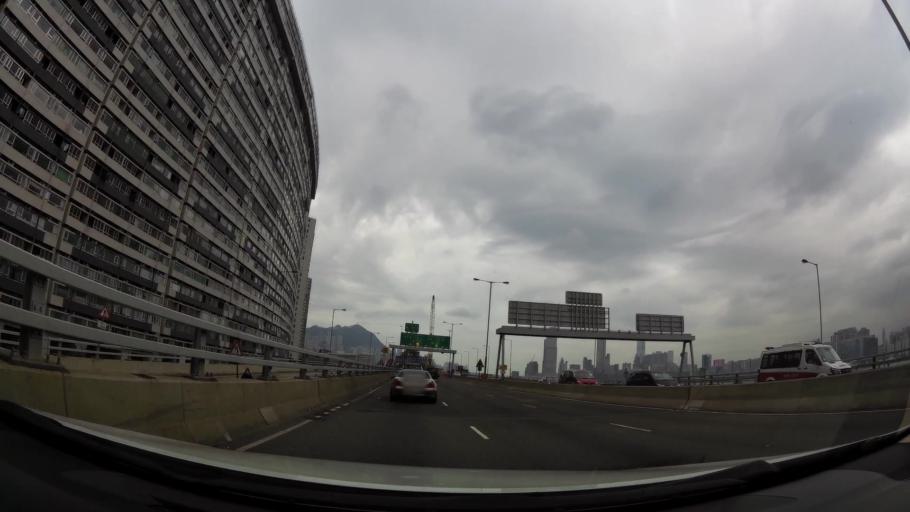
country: HK
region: Kowloon City
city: Kowloon
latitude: 22.2932
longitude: 114.1973
